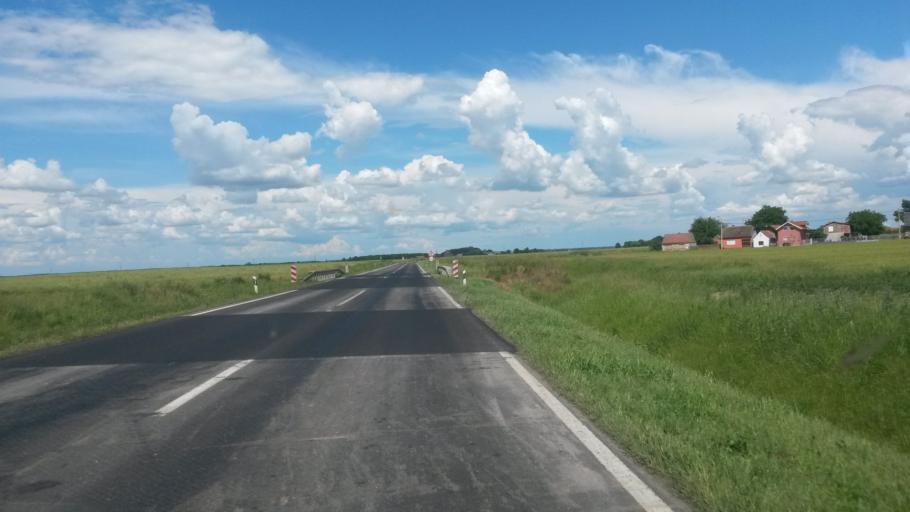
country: HR
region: Osjecko-Baranjska
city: Cepin
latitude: 45.5285
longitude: 18.5445
